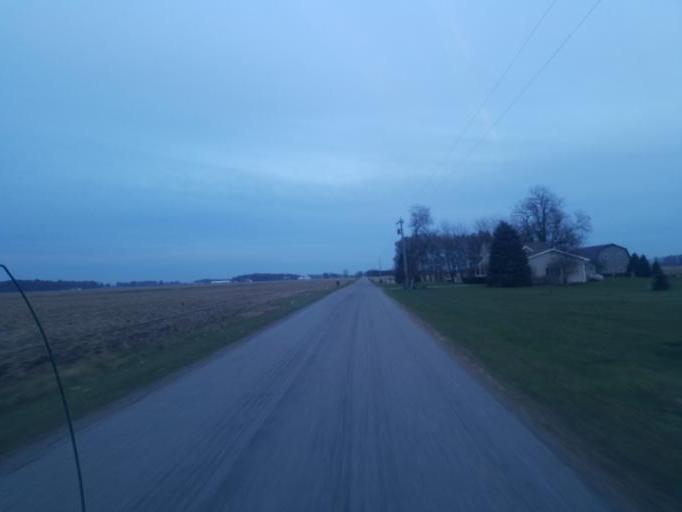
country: US
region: Indiana
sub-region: Adams County
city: Decatur
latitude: 40.7584
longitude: -85.0090
